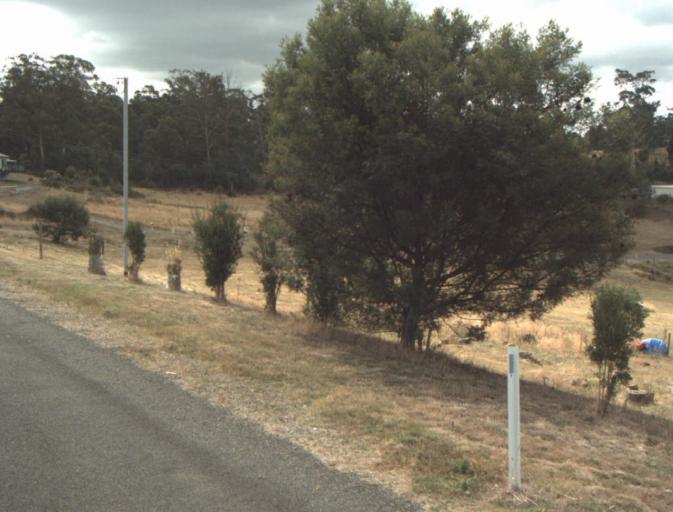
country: AU
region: Tasmania
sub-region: Launceston
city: Mayfield
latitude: -41.3032
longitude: 147.0425
